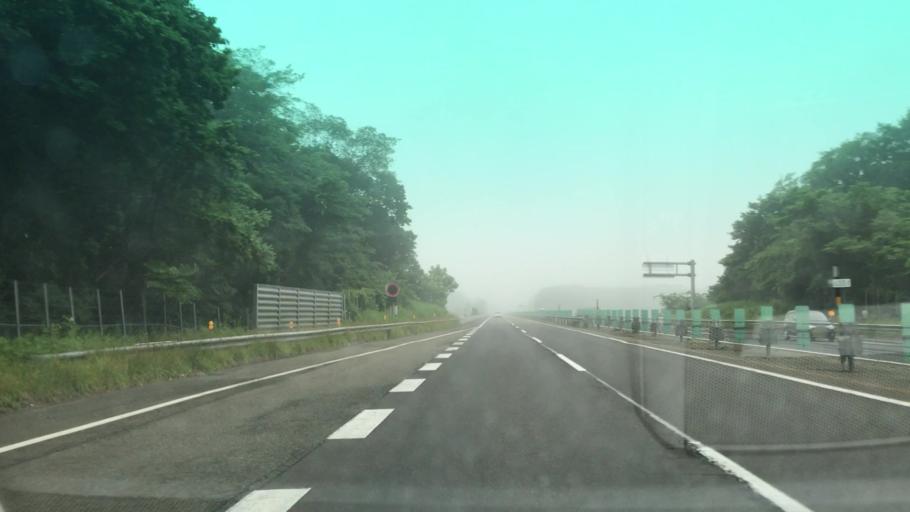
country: JP
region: Hokkaido
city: Chitose
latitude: 42.8089
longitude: 141.6223
